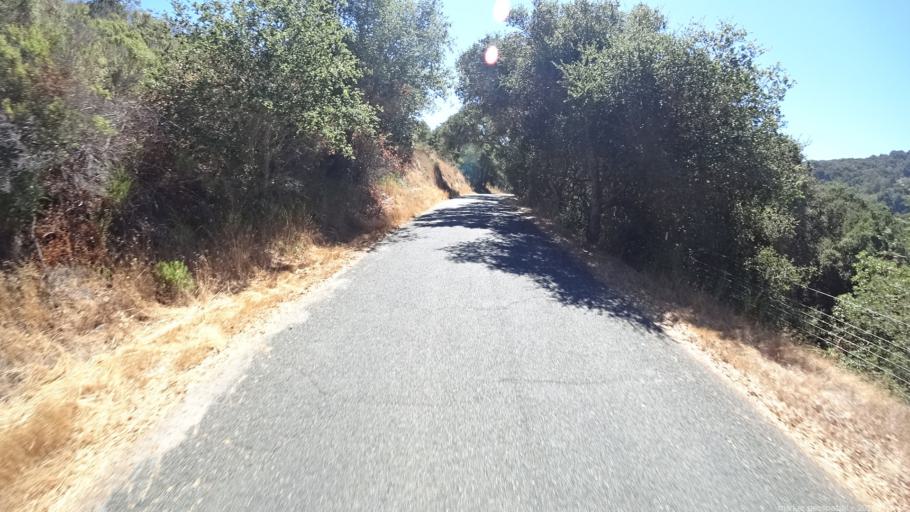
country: US
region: California
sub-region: Monterey County
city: Carmel Valley Village
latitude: 36.4747
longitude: -121.8005
